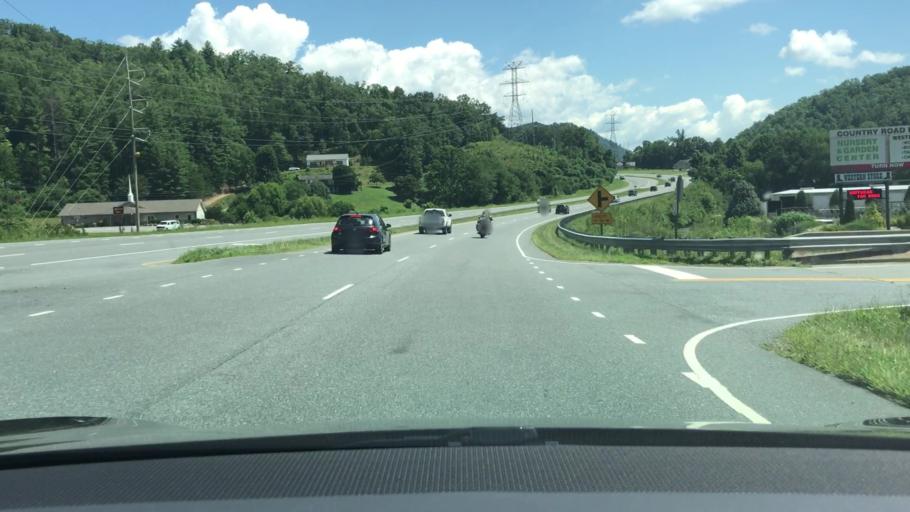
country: US
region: North Carolina
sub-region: Jackson County
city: Sylva
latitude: 35.3338
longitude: -83.2572
